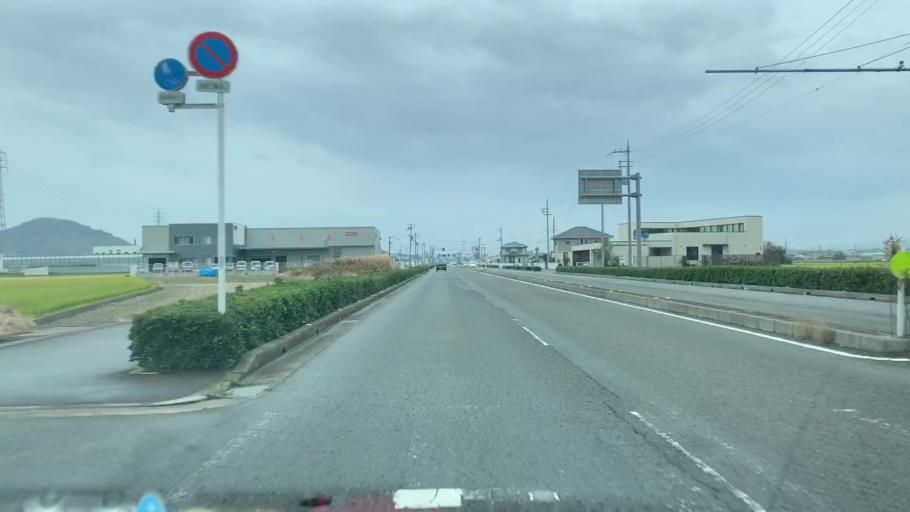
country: JP
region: Wakayama
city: Wakayama-shi
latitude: 34.2388
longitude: 135.2408
